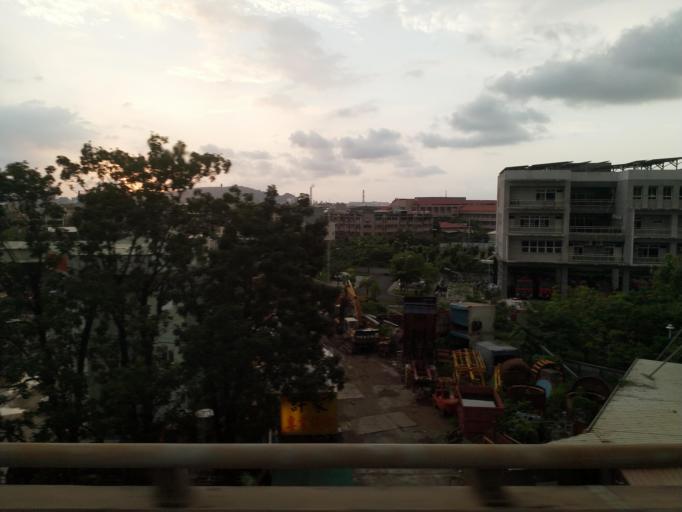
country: TW
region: Taiwan
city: Fengshan
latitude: 22.7008
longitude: 120.3593
